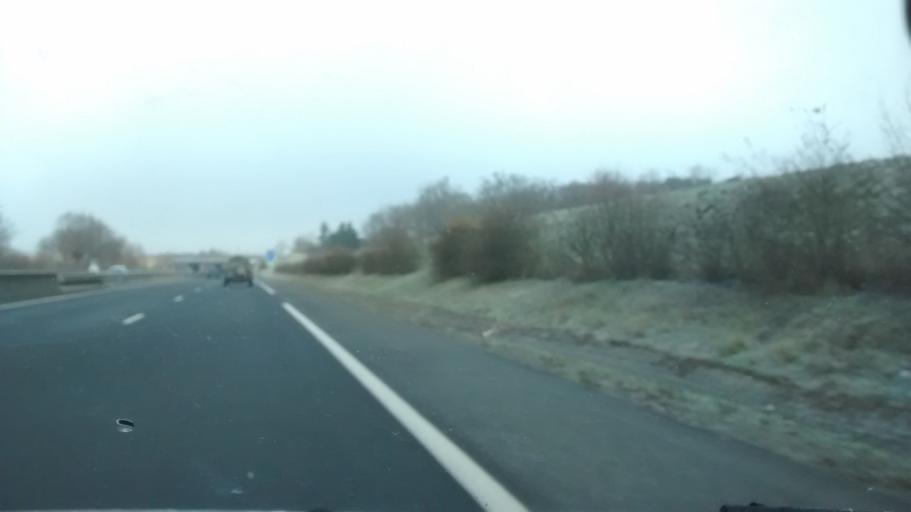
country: FR
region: Centre
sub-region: Departement d'Indre-et-Loire
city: Chambray-les-Tours
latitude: 47.3246
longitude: 0.6955
